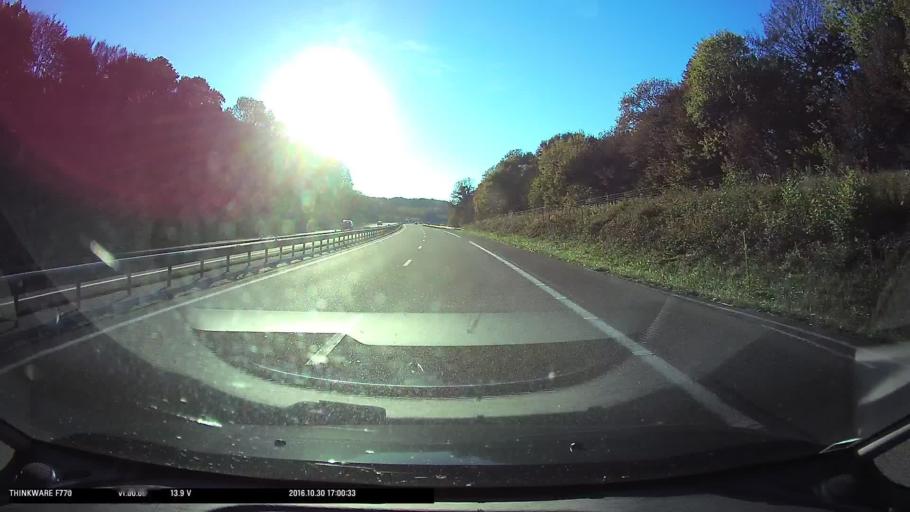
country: FR
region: Franche-Comte
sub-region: Departement du Jura
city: Dampierre
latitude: 47.1859
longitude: 5.7016
